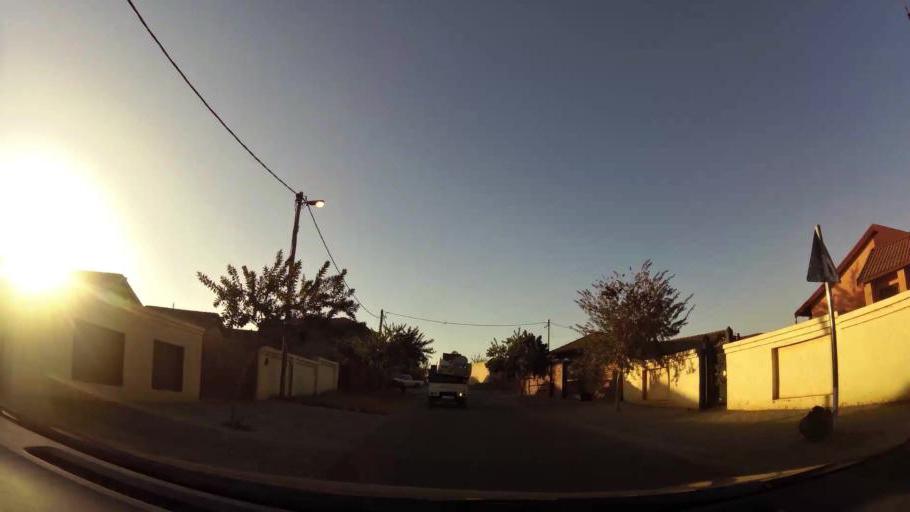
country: ZA
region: Gauteng
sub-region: City of Tshwane Metropolitan Municipality
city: Mabopane
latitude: -25.5835
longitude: 28.1027
